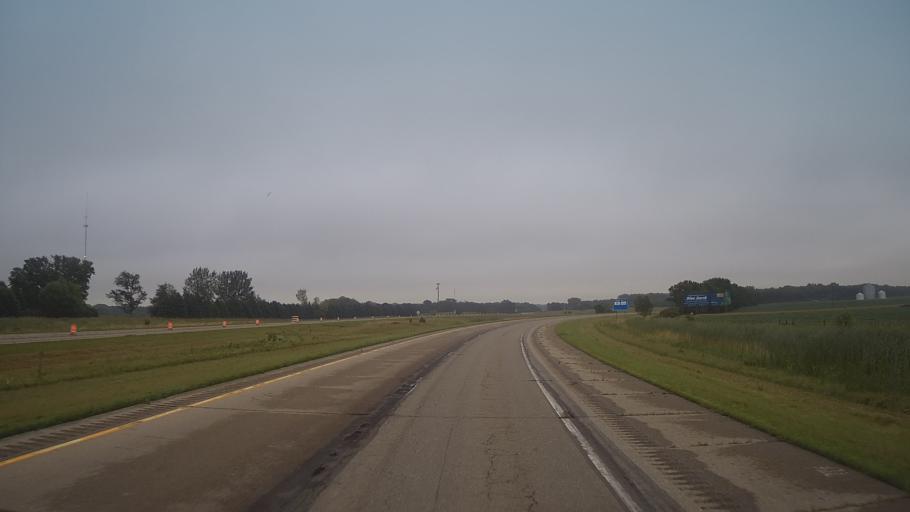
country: US
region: Minnesota
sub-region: Faribault County
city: Blue Earth
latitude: 43.6652
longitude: -94.1308
